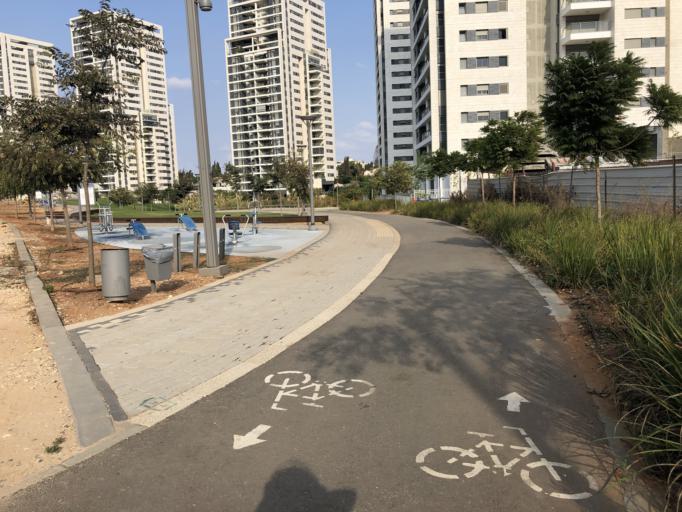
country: IL
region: Tel Aviv
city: Giv`at Shemu'el
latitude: 32.0540
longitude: 34.8438
